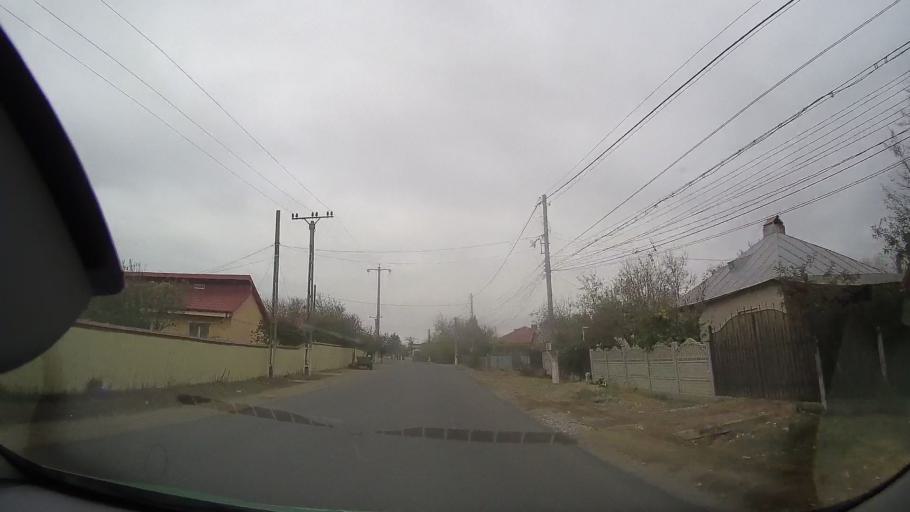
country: RO
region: Braila
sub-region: Comuna Ciresu
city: Ciresu
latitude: 44.9394
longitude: 27.3672
